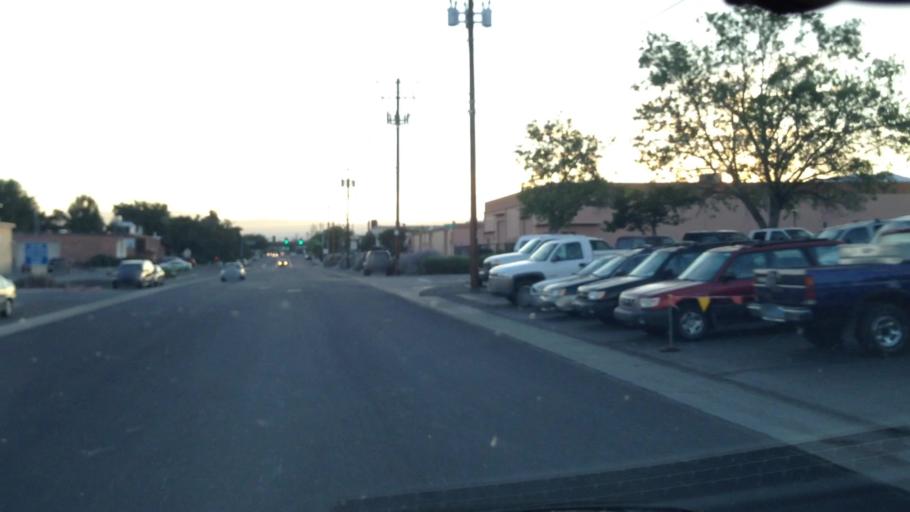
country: US
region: Nevada
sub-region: Washoe County
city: Sparks
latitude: 39.5131
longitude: -119.7748
